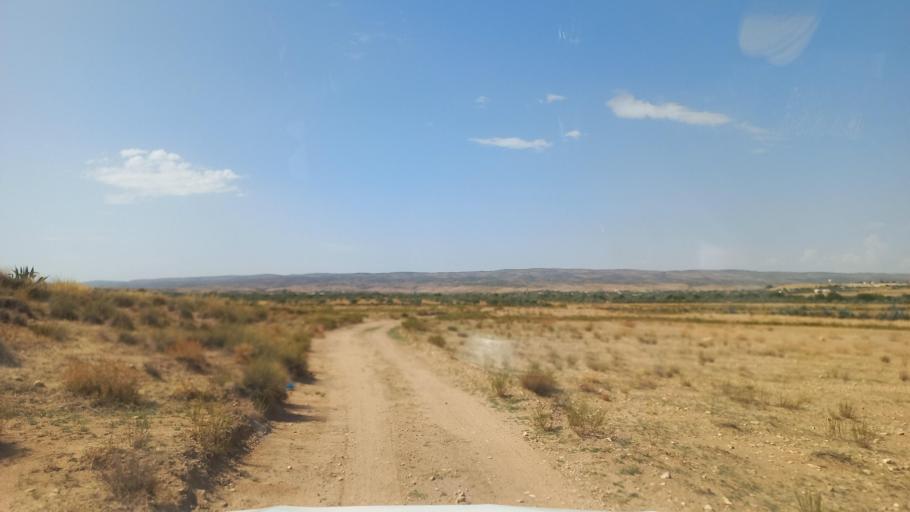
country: TN
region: Al Qasrayn
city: Kasserine
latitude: 35.2556
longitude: 8.9558
